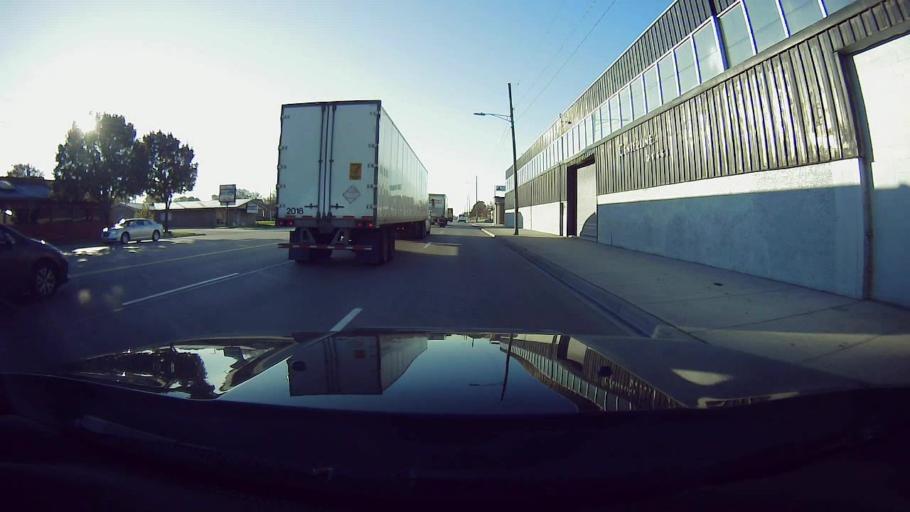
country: US
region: Michigan
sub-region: Macomb County
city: Center Line
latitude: 42.5043
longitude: -83.0284
